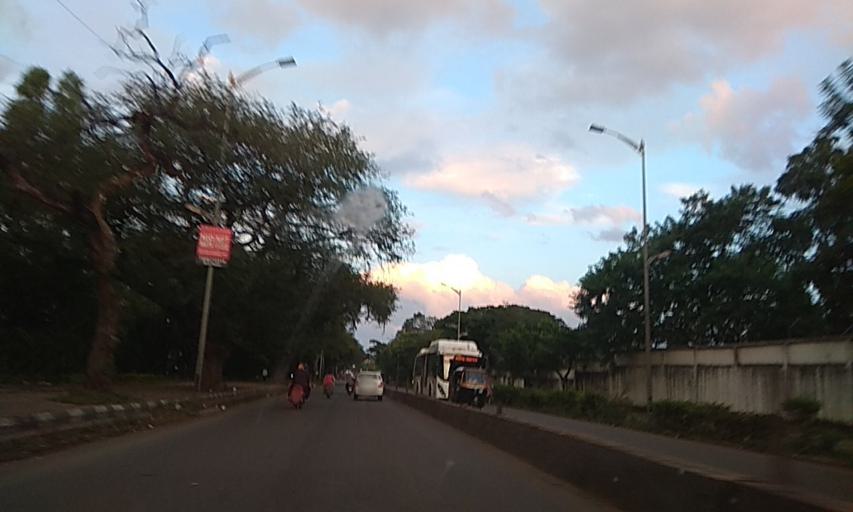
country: IN
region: Maharashtra
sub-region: Pune Division
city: Pune
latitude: 18.5069
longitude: 73.8916
